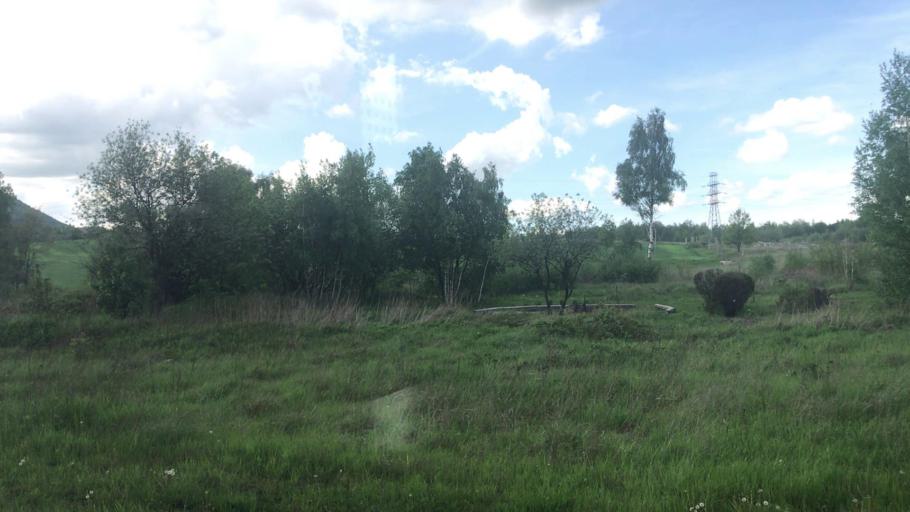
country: PL
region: Lower Silesian Voivodeship
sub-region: Powiat walbrzyski
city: Walbrzych
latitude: 50.7695
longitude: 16.2572
